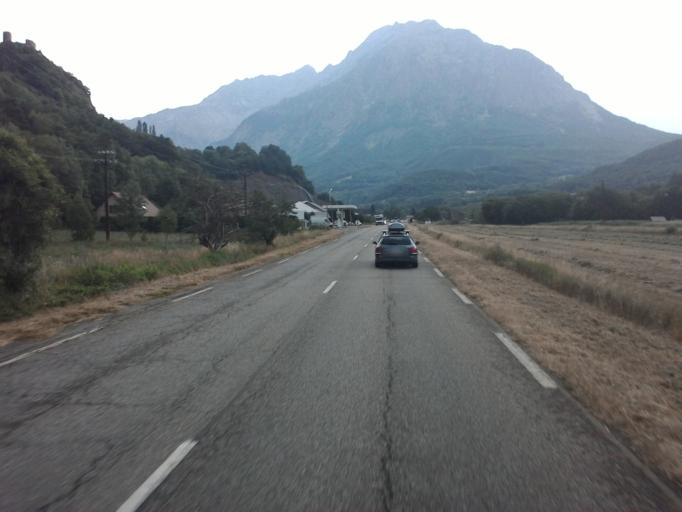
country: FR
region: Provence-Alpes-Cote d'Azur
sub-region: Departement des Hautes-Alpes
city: Saint-Bonnet-en-Champsaur
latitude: 44.7770
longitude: 6.0118
